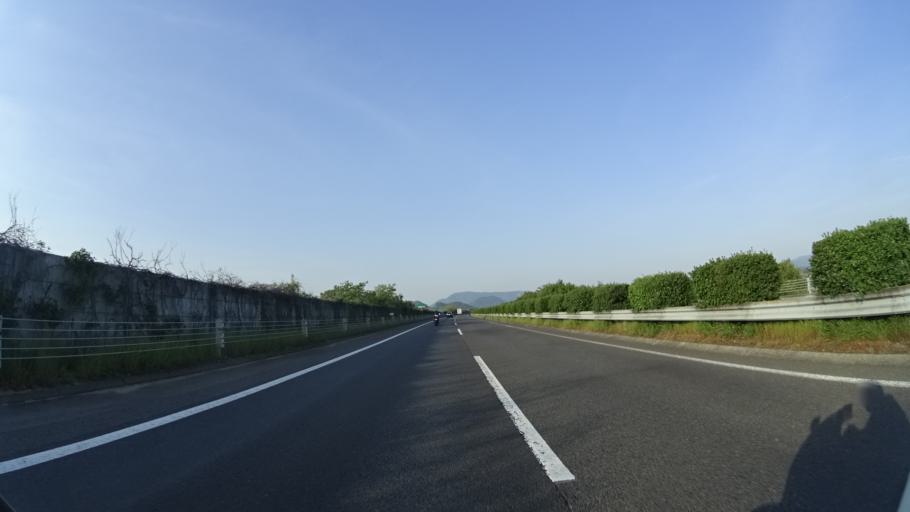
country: JP
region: Kagawa
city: Kan'onjicho
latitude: 34.1246
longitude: 133.6957
